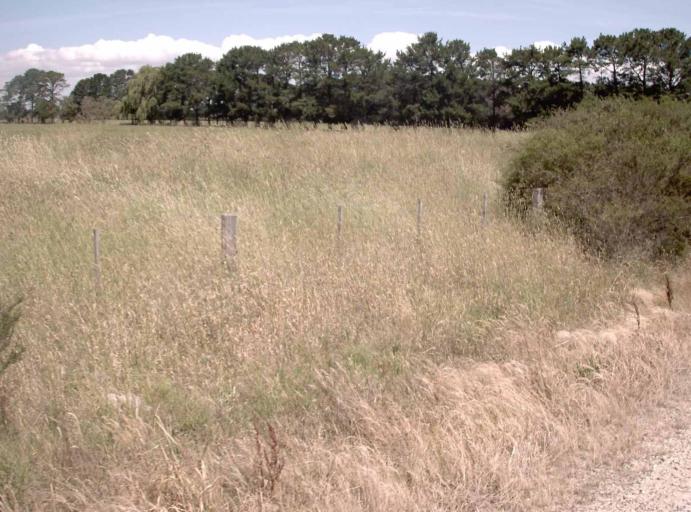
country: AU
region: Victoria
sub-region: Wellington
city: Heyfield
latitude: -38.0342
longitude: 146.8785
